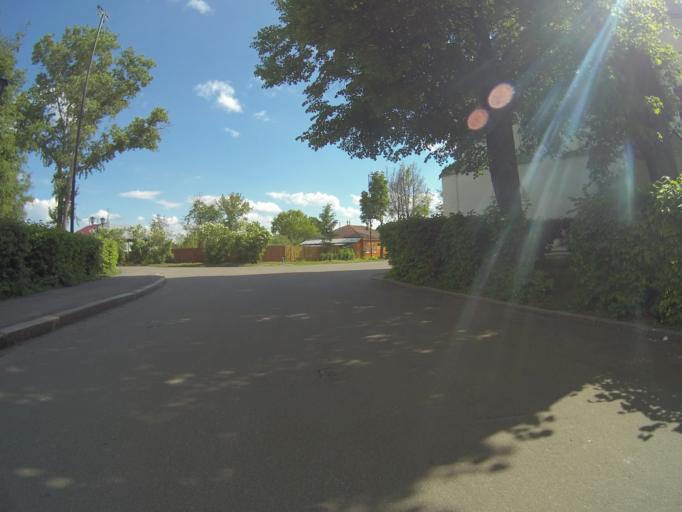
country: RU
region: Vladimir
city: Suzdal'
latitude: 56.4165
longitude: 40.4437
